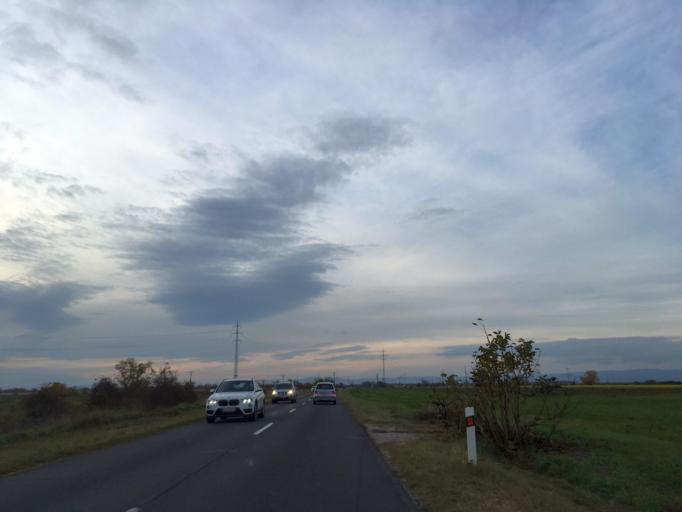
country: SK
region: Bratislavsky
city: Dunajska Luzna
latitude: 48.1107
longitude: 17.3247
